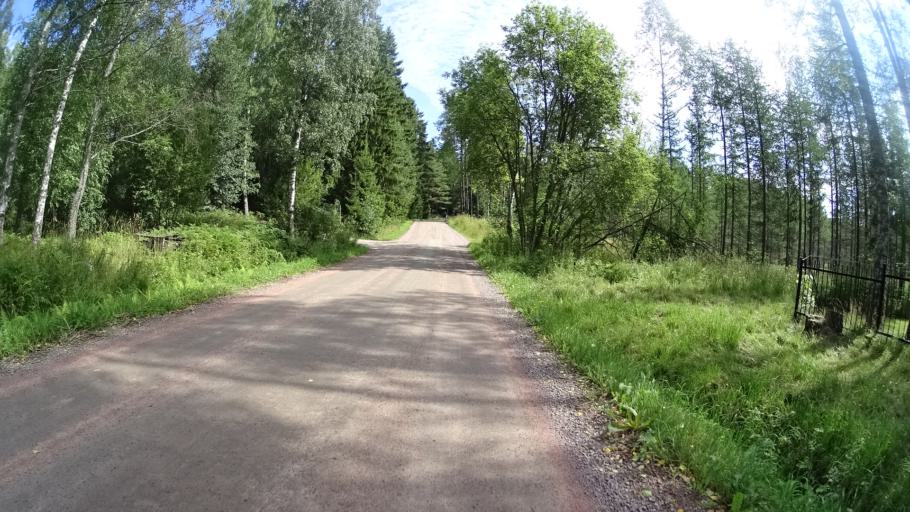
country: FI
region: Uusimaa
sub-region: Helsinki
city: Kirkkonummi
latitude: 60.1012
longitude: 24.5578
